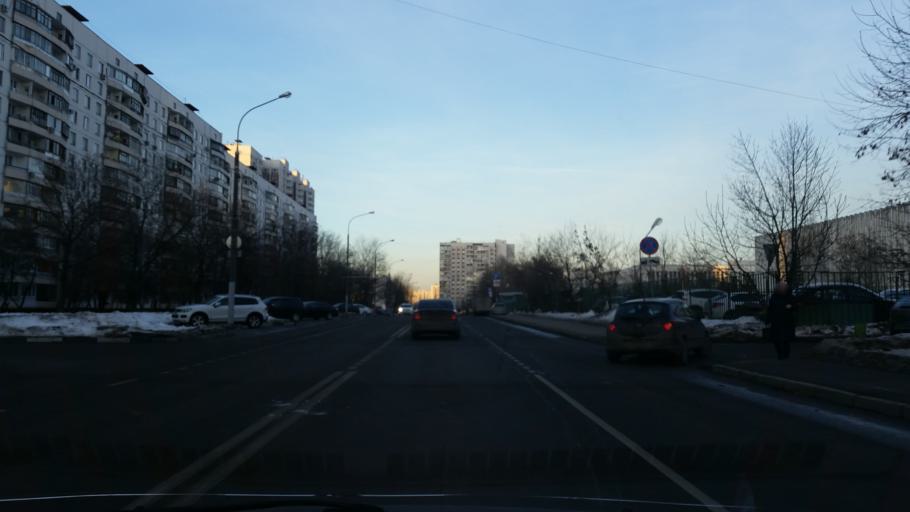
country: RU
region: Moscow
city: Nagornyy
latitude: 55.6295
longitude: 37.6122
